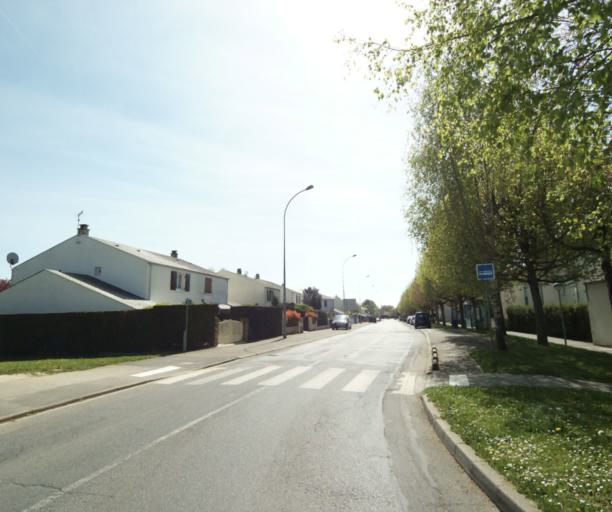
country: FR
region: Ile-de-France
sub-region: Departement de Seine-et-Marne
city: Nangis
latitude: 48.5532
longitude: 3.0077
